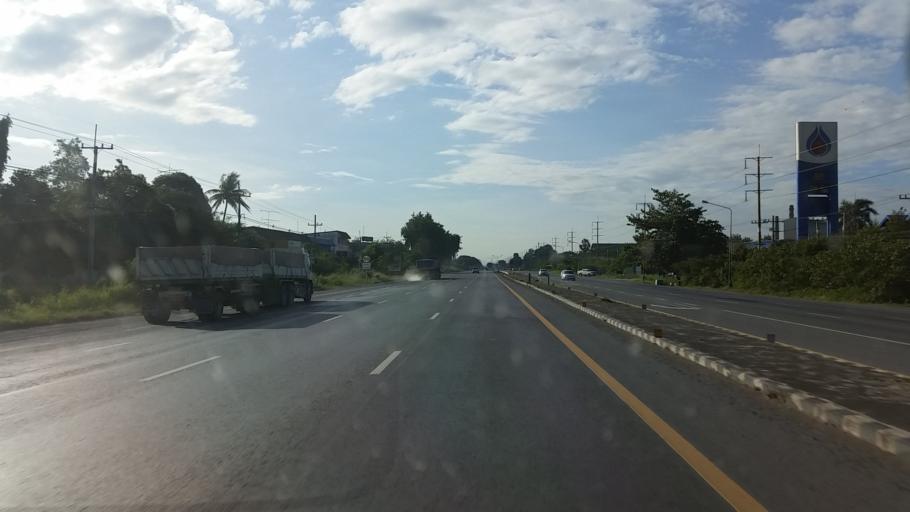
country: TH
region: Sara Buri
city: Chaloem Phra Kiat
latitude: 14.6366
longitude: 100.8877
